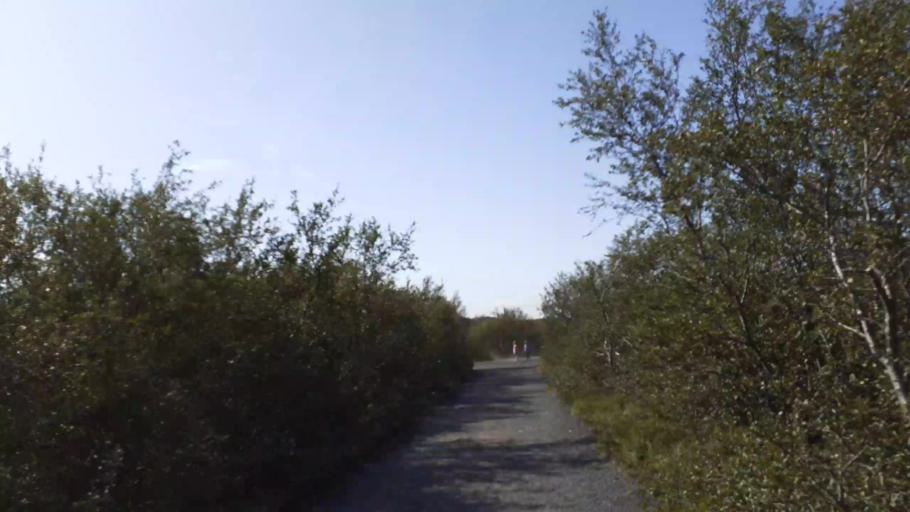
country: IS
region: West
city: Borgarnes
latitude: 64.7542
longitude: -21.5481
